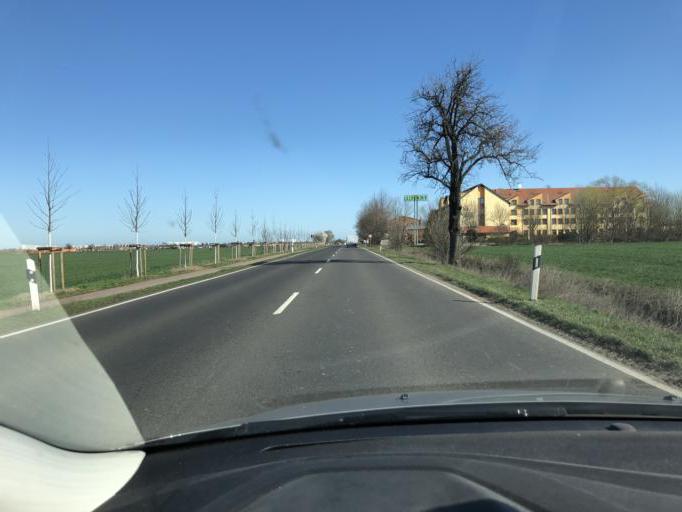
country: DE
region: Saxony-Anhalt
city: Magdeburg
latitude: 52.0662
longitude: 11.6146
